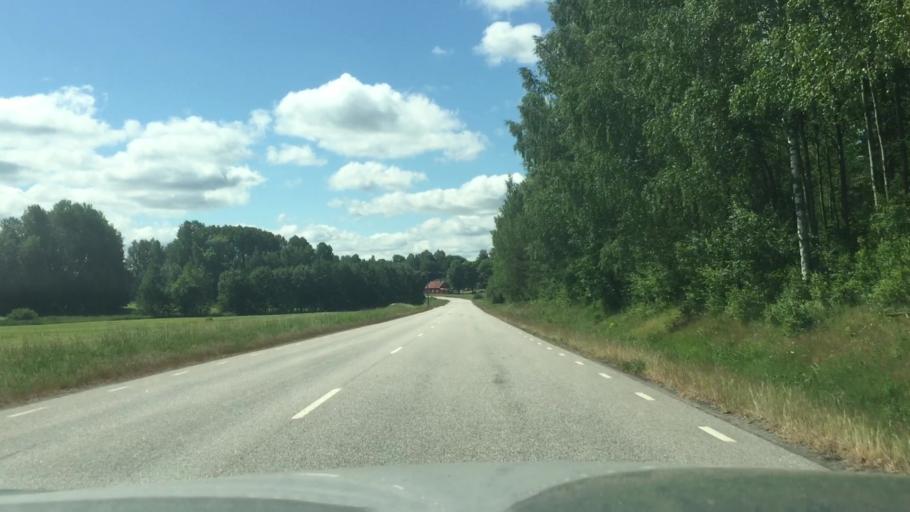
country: SE
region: Vaestra Goetaland
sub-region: Karlsborgs Kommun
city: Molltorp
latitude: 58.6340
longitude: 14.3918
